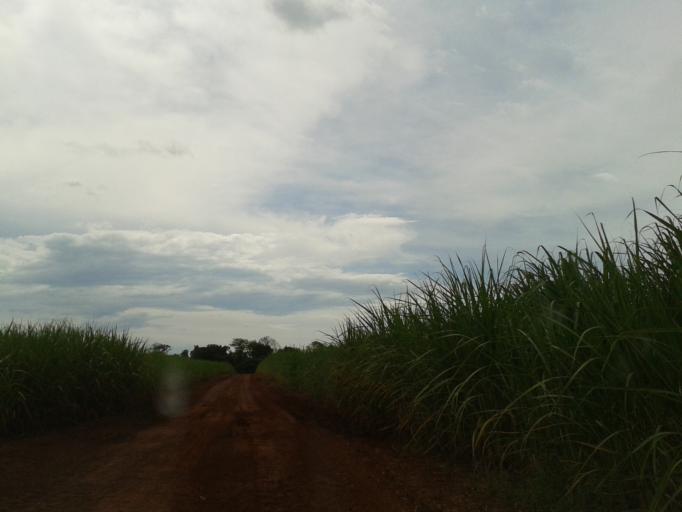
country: BR
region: Minas Gerais
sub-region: Centralina
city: Centralina
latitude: -18.6624
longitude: -49.2529
